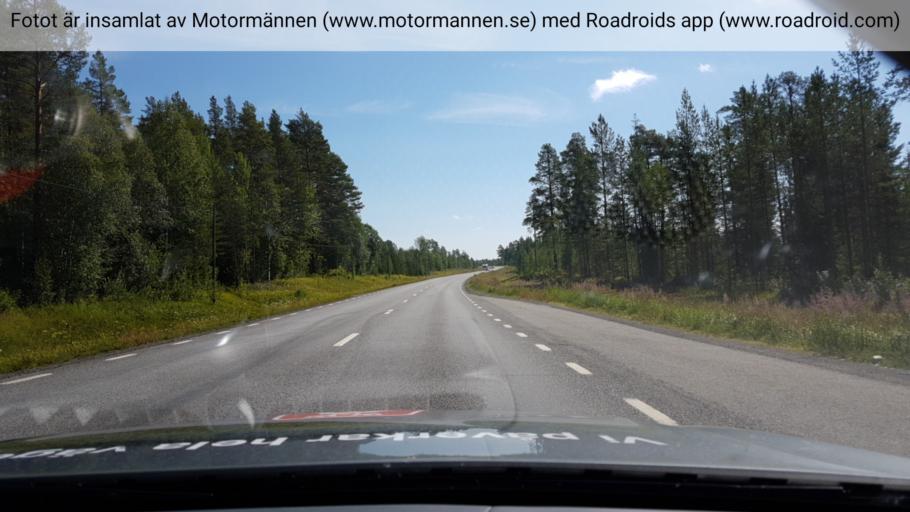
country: SE
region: Jaemtland
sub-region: OEstersunds Kommun
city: Lit
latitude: 63.3910
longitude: 14.9296
